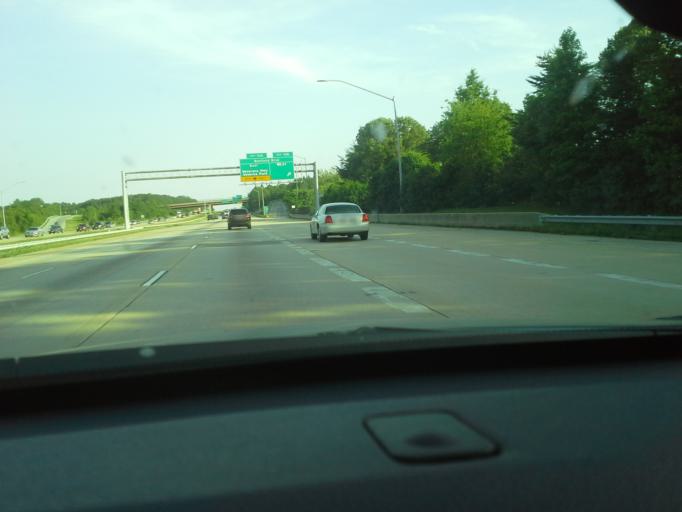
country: US
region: Maryland
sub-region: Anne Arundel County
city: South Gate
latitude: 39.0996
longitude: -76.6285
